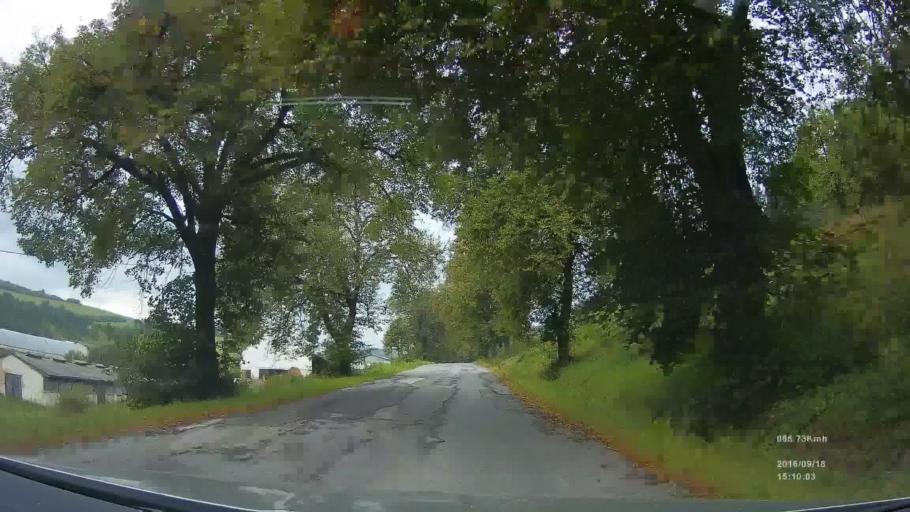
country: SK
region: Presovsky
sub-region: Okres Presov
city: Levoca
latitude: 49.0181
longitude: 20.5039
